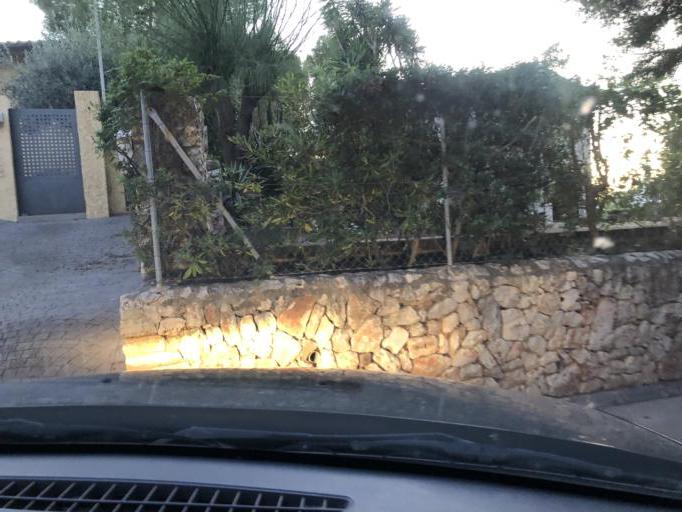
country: ES
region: Balearic Islands
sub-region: Illes Balears
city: Santa Ponsa
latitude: 39.5264
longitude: 2.4849
